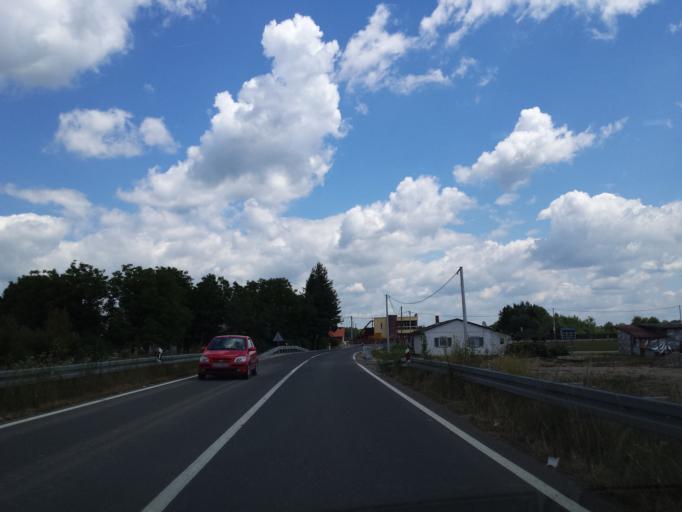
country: HR
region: Sisacko-Moslavacka
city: Lekenik
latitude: 45.5690
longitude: 16.2233
